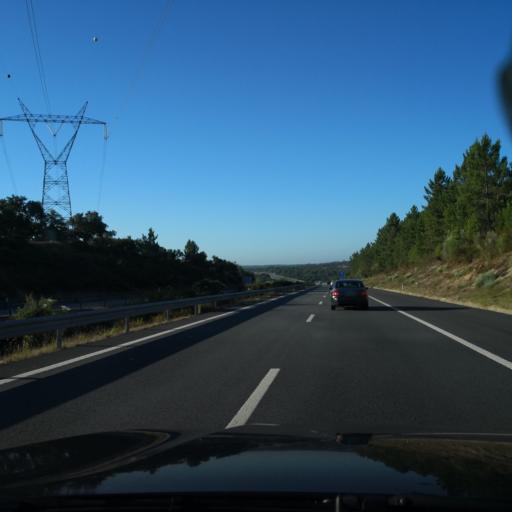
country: PT
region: Setubal
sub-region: Alcacer do Sal
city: Alcacer do Sal
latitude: 38.4434
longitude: -8.5247
